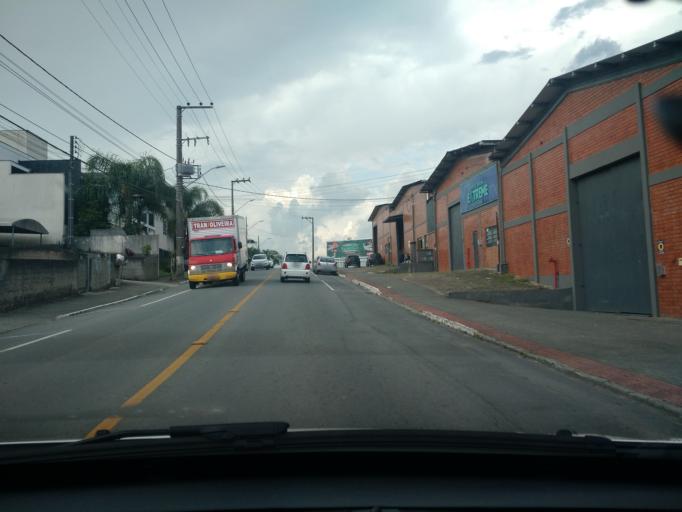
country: BR
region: Santa Catarina
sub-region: Jaragua Do Sul
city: Jaragua do Sul
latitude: -26.4908
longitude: -49.0912
